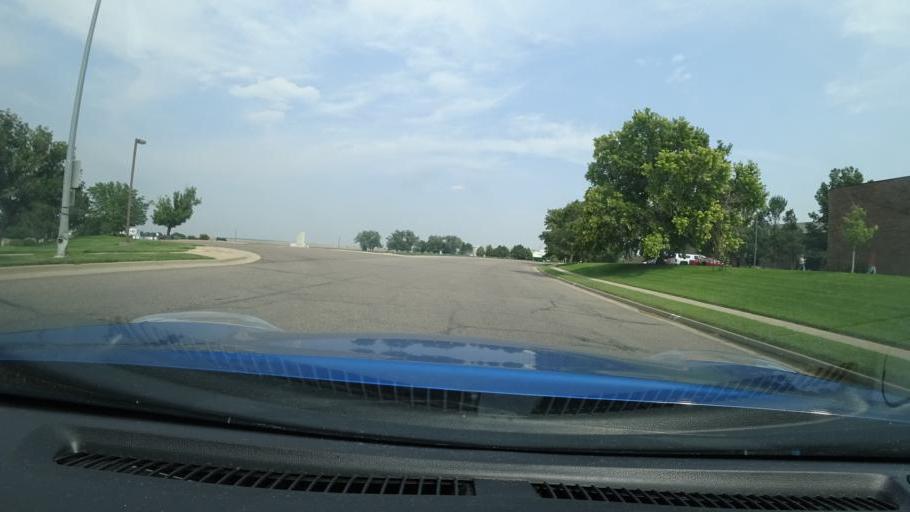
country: US
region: Colorado
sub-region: Adams County
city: Aurora
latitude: 39.7588
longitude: -104.7444
